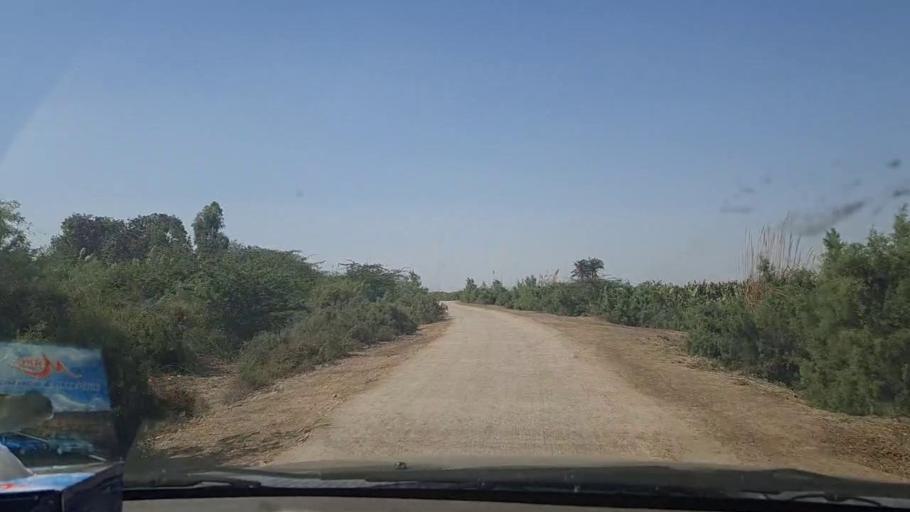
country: PK
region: Sindh
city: Chuhar Jamali
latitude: 24.2860
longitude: 67.7590
